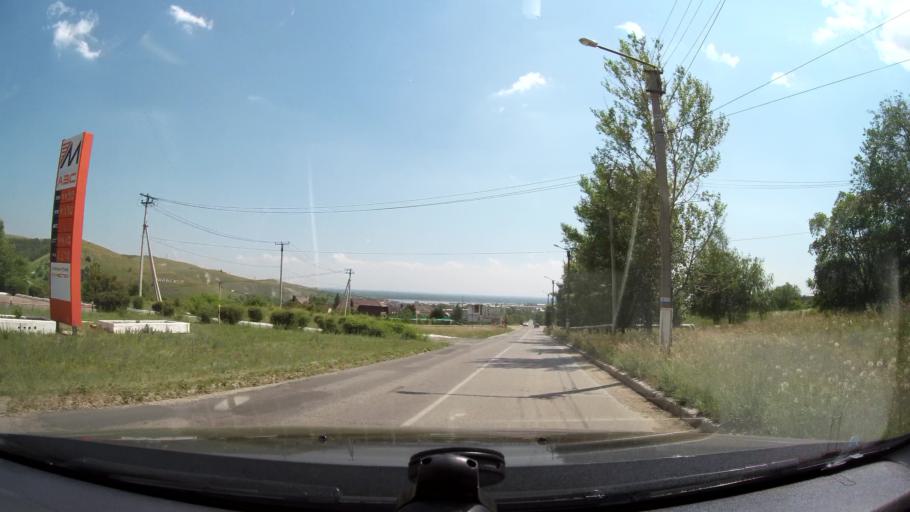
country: RU
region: Saratov
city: Vol'sk
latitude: 52.0658
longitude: 47.3771
